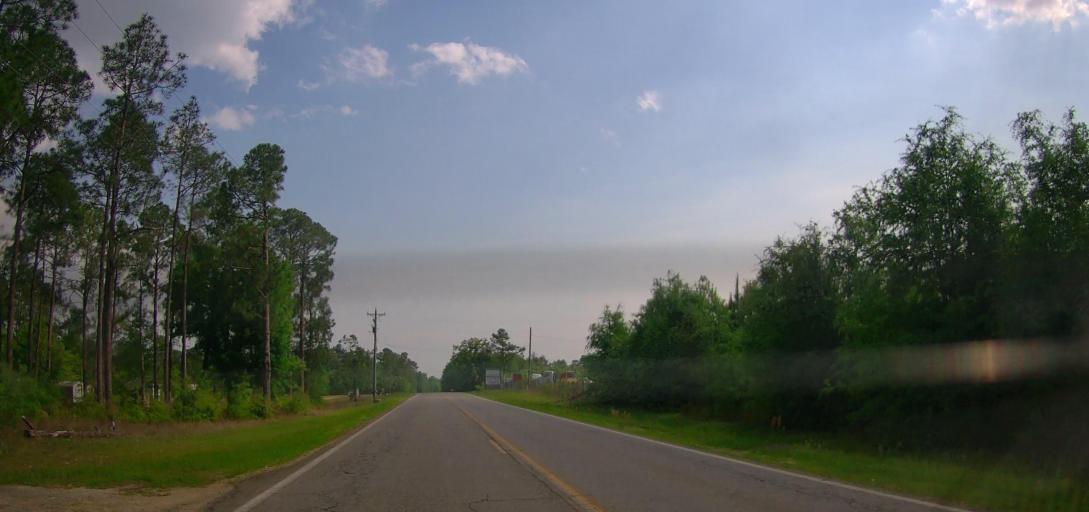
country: US
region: Georgia
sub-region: Laurens County
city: East Dublin
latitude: 32.5873
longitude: -82.8647
